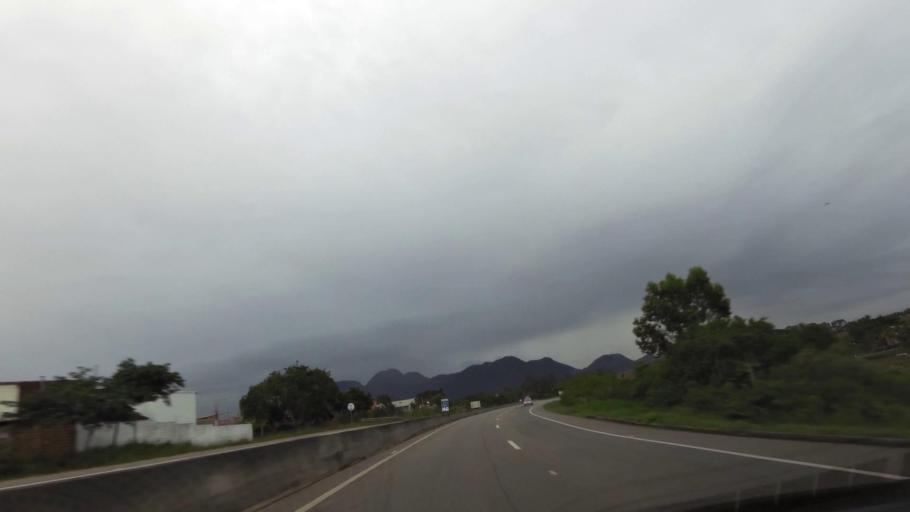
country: BR
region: Espirito Santo
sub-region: Guarapari
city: Guarapari
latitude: -20.6138
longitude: -40.4543
